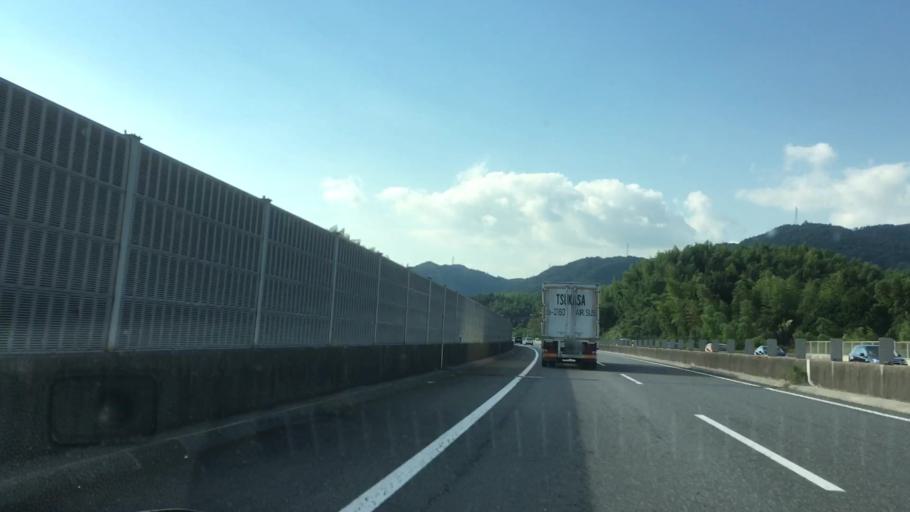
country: JP
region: Yamaguchi
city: Kudamatsu
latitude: 34.0392
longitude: 131.9224
